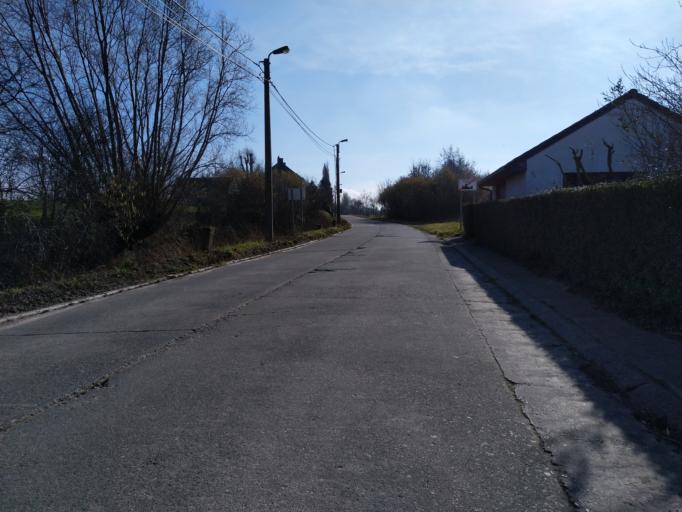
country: BE
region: Wallonia
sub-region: Province du Hainaut
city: Quevy-le-Petit
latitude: 50.3501
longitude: 3.8976
